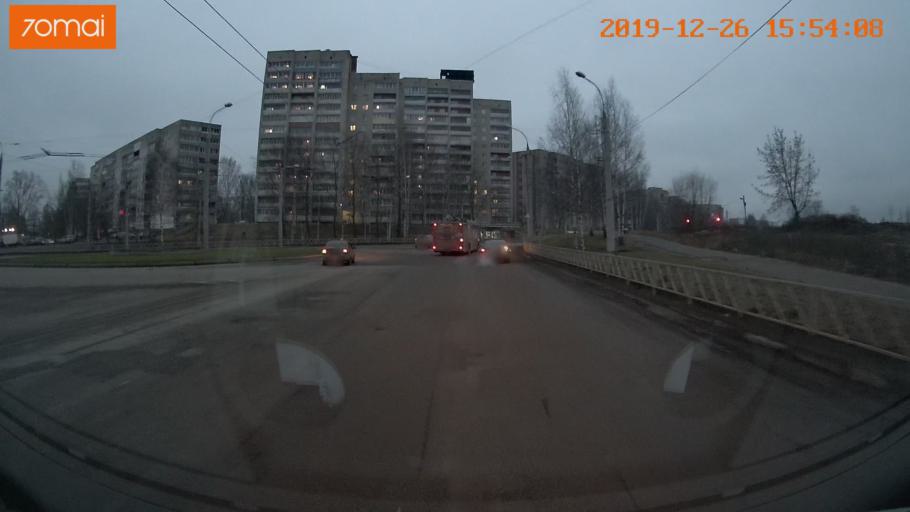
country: RU
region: Jaroslavl
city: Rybinsk
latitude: 58.0462
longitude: 38.8211
